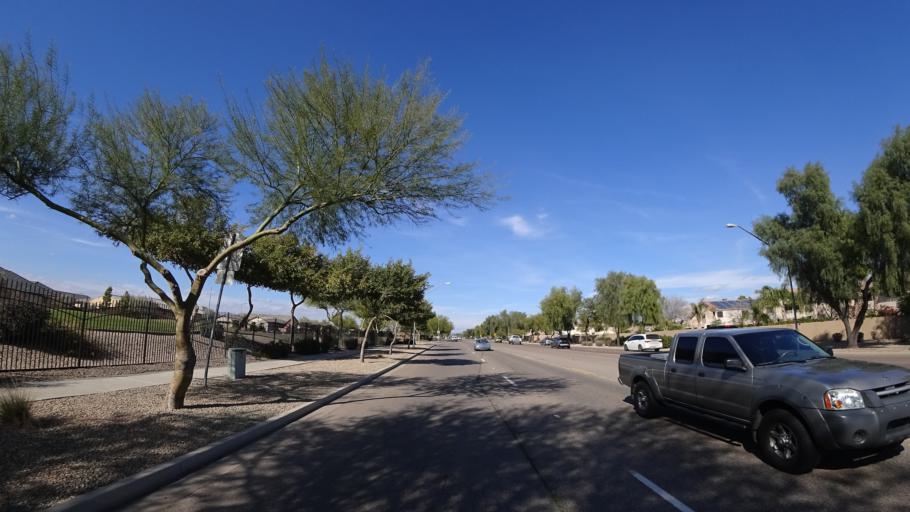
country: US
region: Arizona
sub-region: Maricopa County
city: Sun City
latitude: 33.6761
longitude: -112.2205
